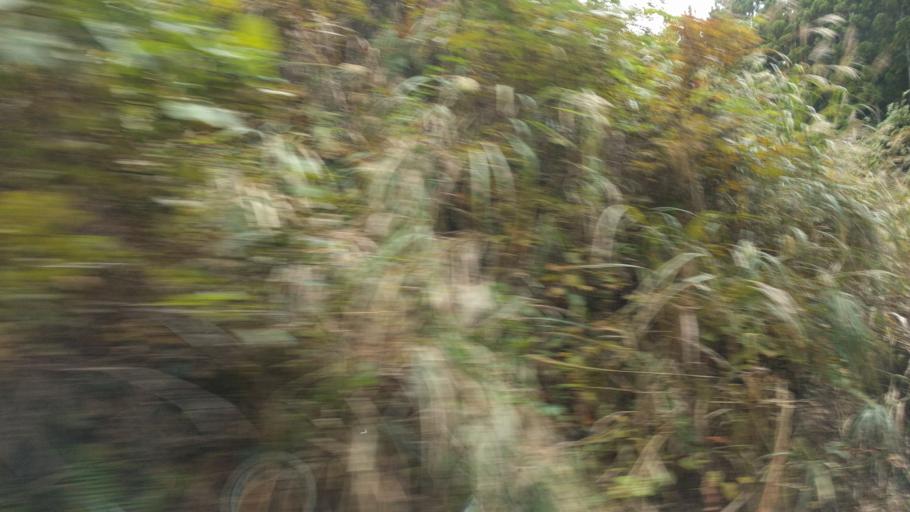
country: JP
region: Fukushima
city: Kitakata
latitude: 37.4303
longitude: 139.7924
